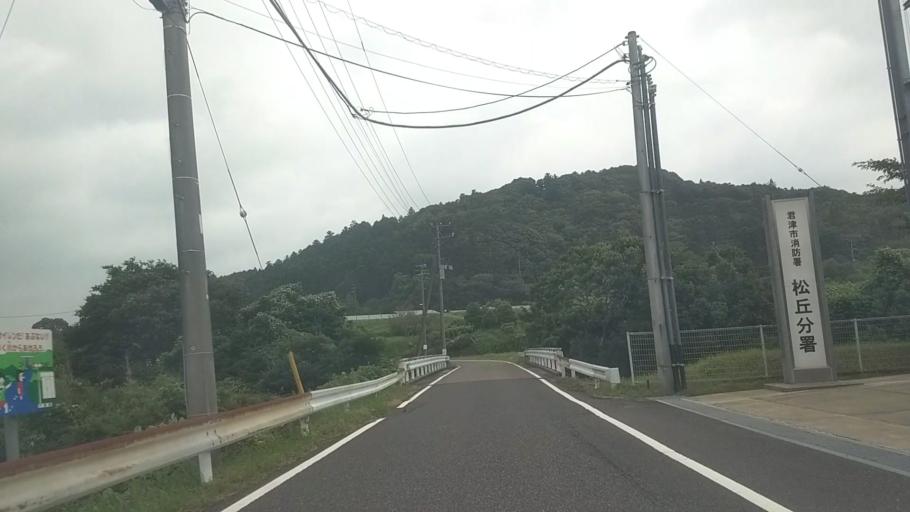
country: JP
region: Chiba
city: Kawaguchi
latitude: 35.2601
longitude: 140.0575
